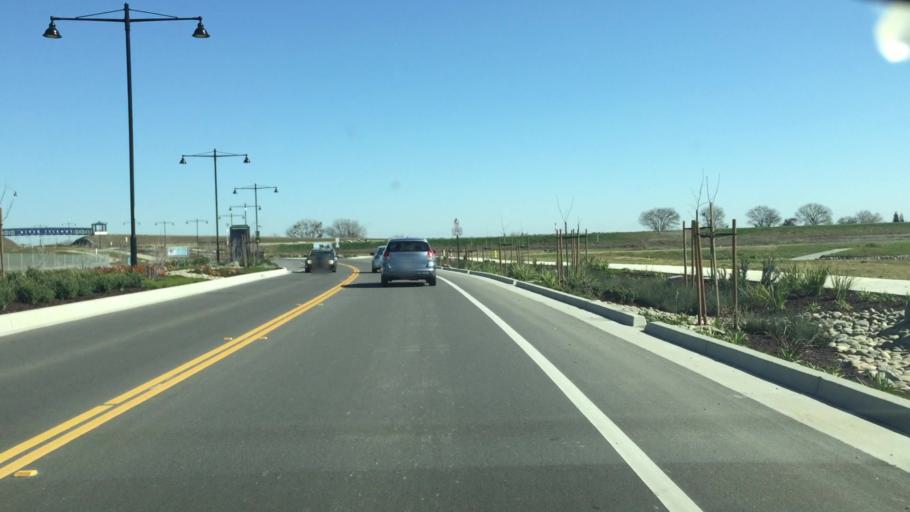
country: US
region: California
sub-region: San Joaquin County
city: Lathrop
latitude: 37.8011
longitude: -121.3181
